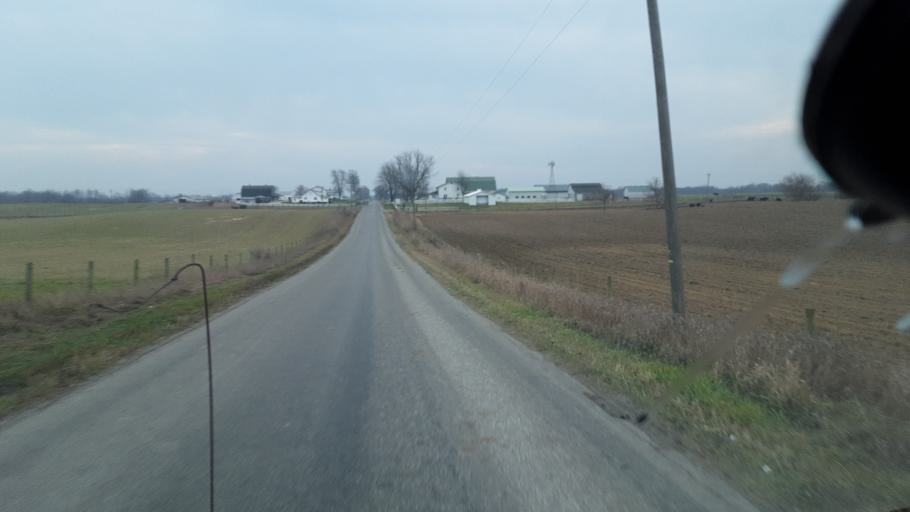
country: US
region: Indiana
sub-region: Elkhart County
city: Middlebury
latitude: 41.7071
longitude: -85.6204
